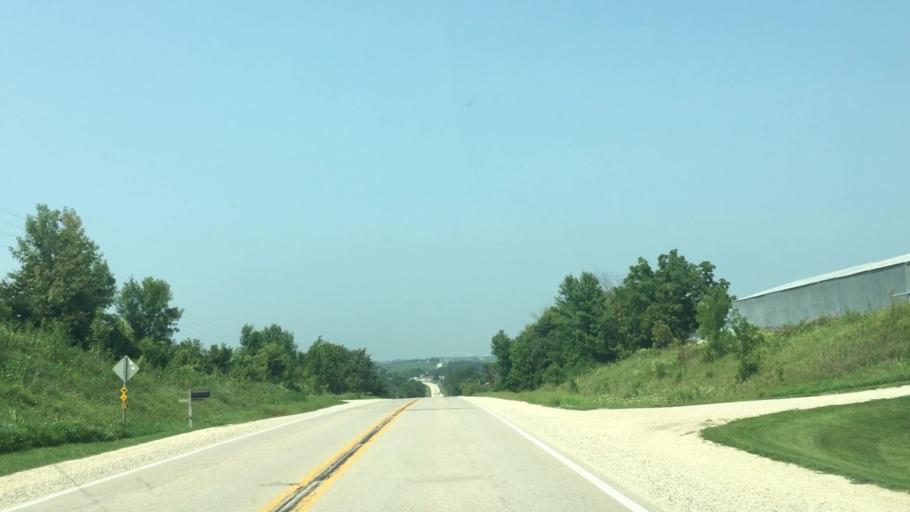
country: US
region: Iowa
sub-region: Fayette County
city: West Union
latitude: 43.1032
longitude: -91.8691
